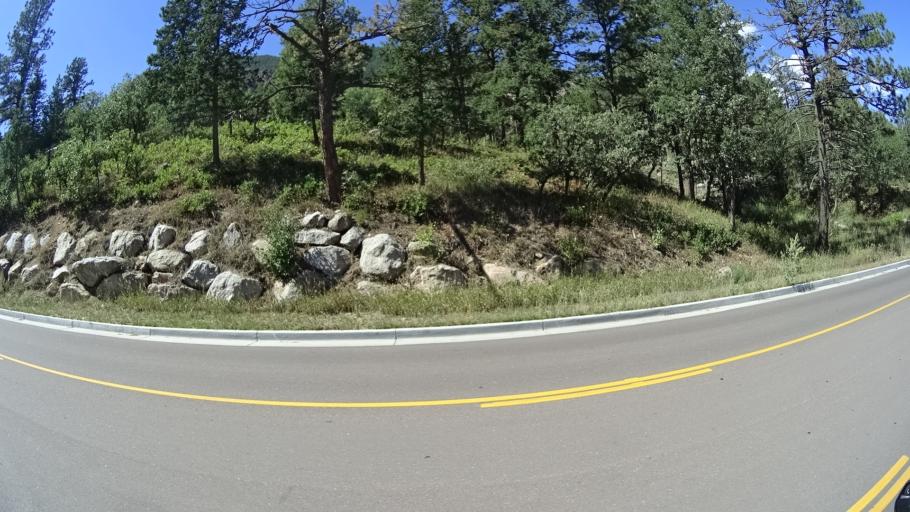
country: US
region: Colorado
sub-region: El Paso County
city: Colorado Springs
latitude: 38.7728
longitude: -104.8533
